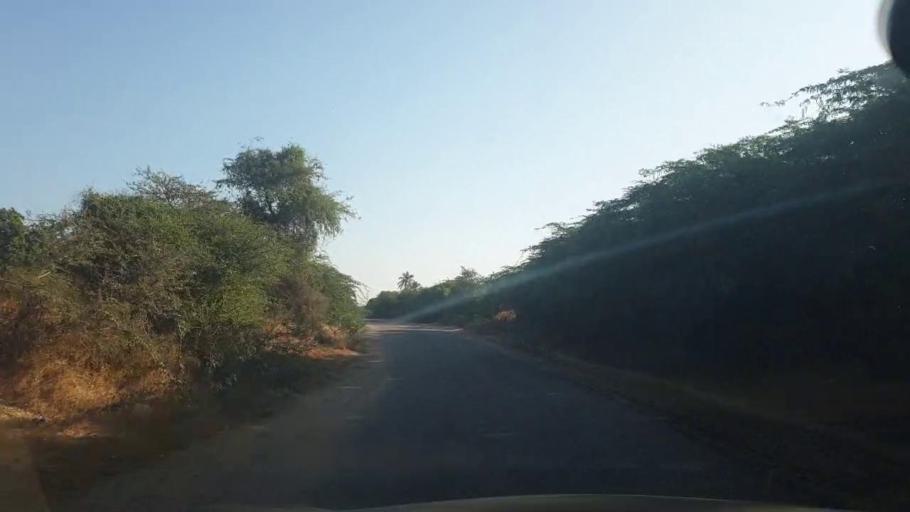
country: PK
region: Sindh
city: Malir Cantonment
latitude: 25.1162
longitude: 67.2760
